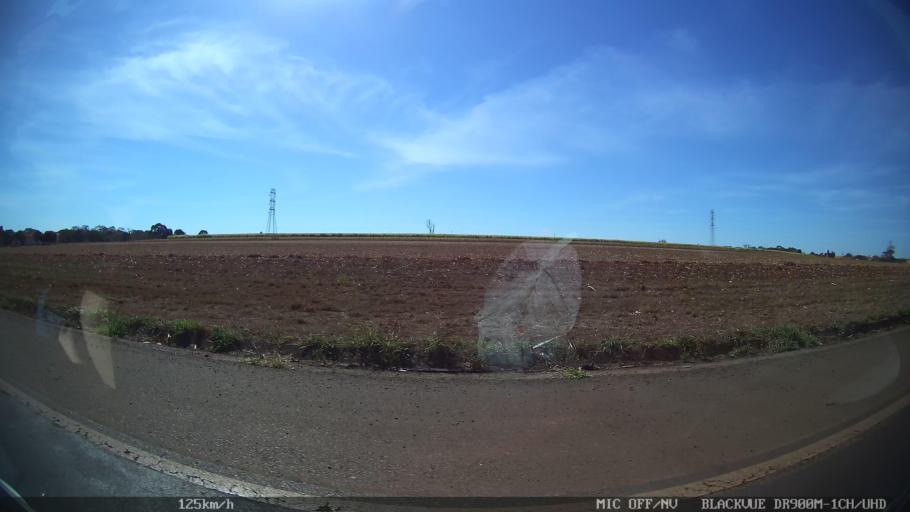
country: BR
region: Sao Paulo
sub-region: Ipua
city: Ipua
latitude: -20.4522
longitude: -48.1713
